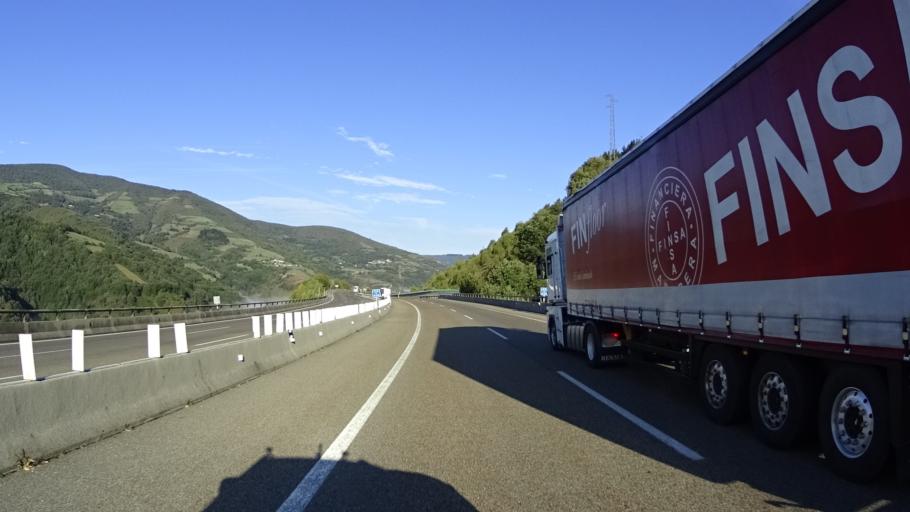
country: ES
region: Galicia
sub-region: Provincia de Lugo
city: San Roman
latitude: 42.7495
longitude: -7.0591
